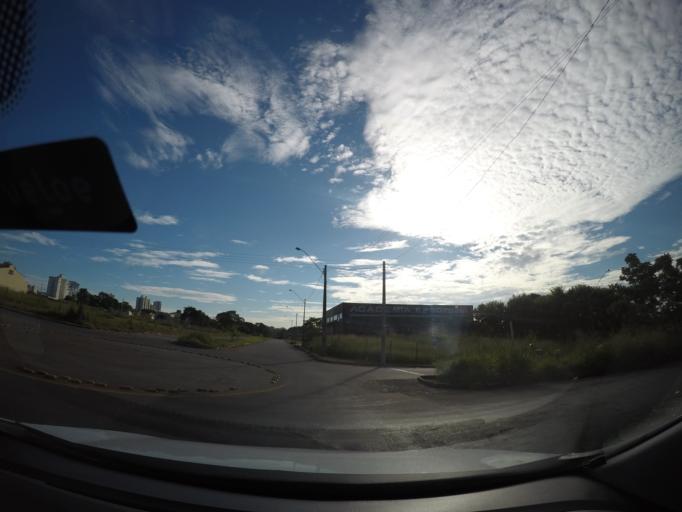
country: BR
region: Goias
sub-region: Goiania
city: Goiania
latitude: -16.7462
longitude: -49.2729
